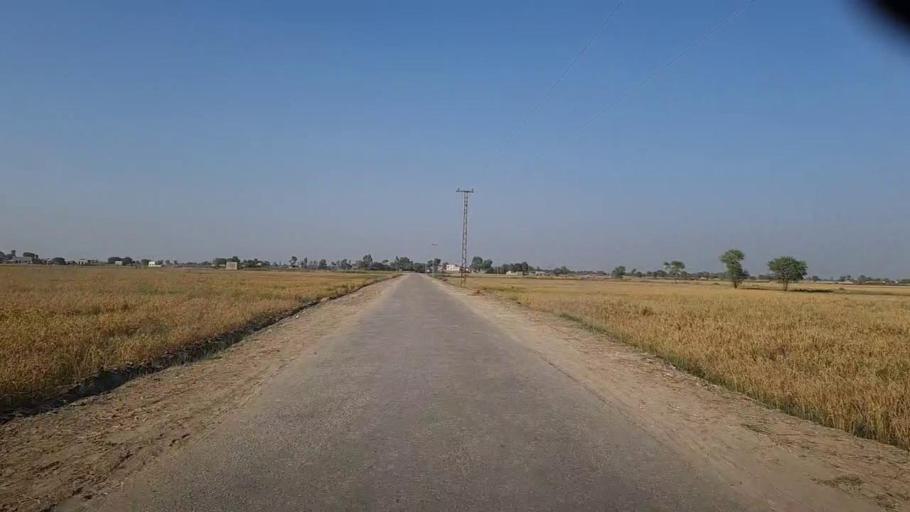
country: PK
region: Sindh
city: Tangwani
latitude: 28.2894
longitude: 68.9516
